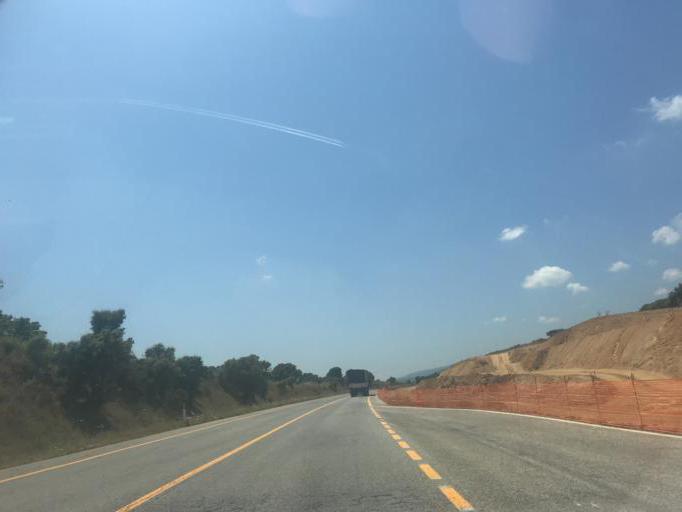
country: IT
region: Sardinia
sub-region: Provincia di Olbia-Tempio
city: Berchidda
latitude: 40.7788
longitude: 9.2367
